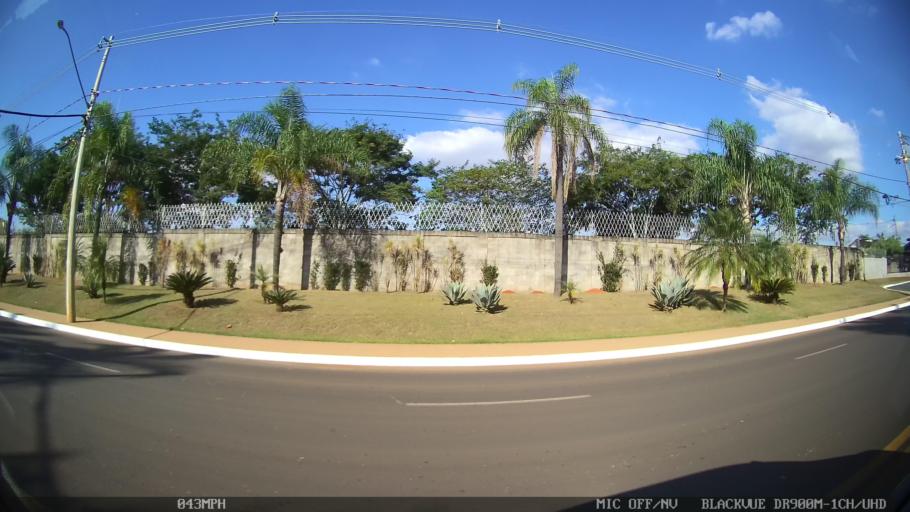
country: BR
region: Sao Paulo
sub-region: Nova Odessa
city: Nova Odessa
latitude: -22.8052
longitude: -47.3187
